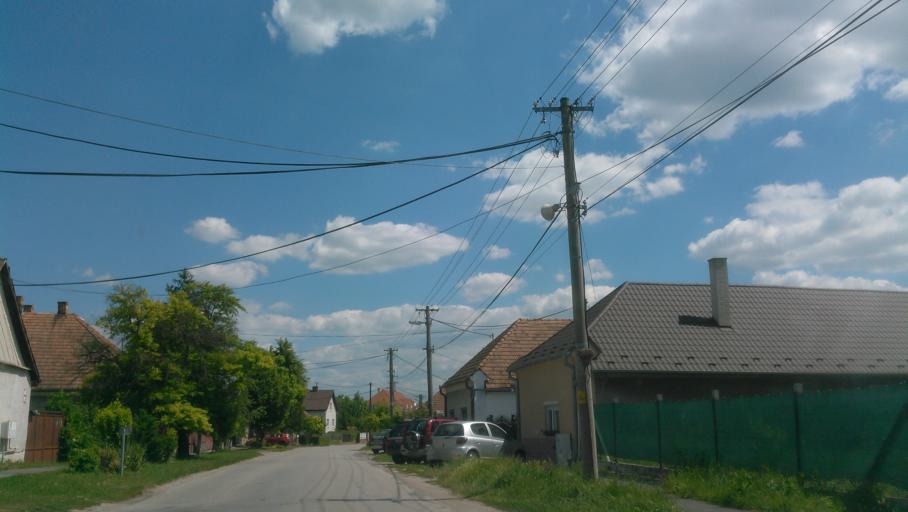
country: SK
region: Trnavsky
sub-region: Okres Dunajska Streda
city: Velky Meder
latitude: 47.8853
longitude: 17.8099
